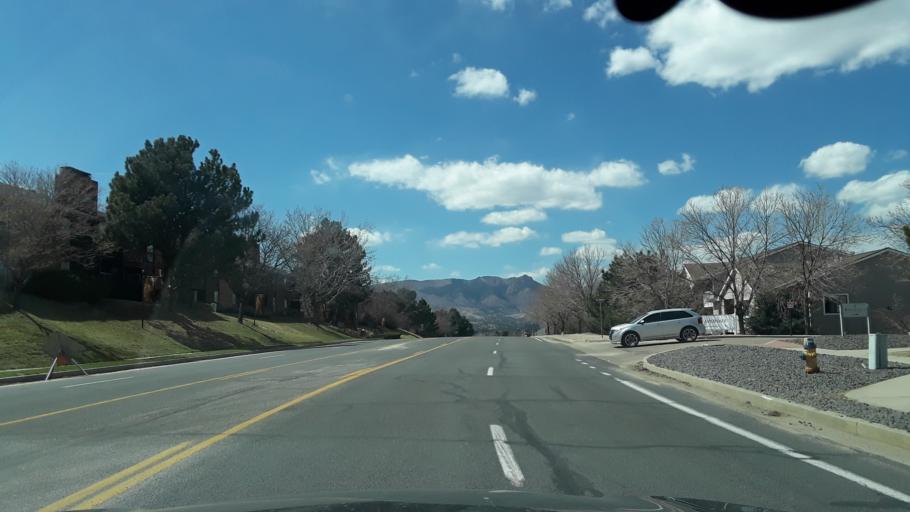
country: US
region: Colorado
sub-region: El Paso County
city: Colorado Springs
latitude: 38.9142
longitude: -104.7767
